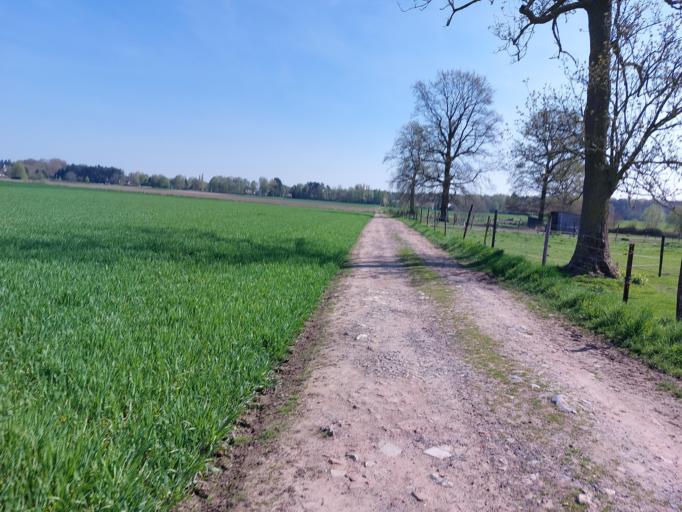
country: BE
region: Wallonia
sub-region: Province du Hainaut
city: Jurbise
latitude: 50.5168
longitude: 3.9126
